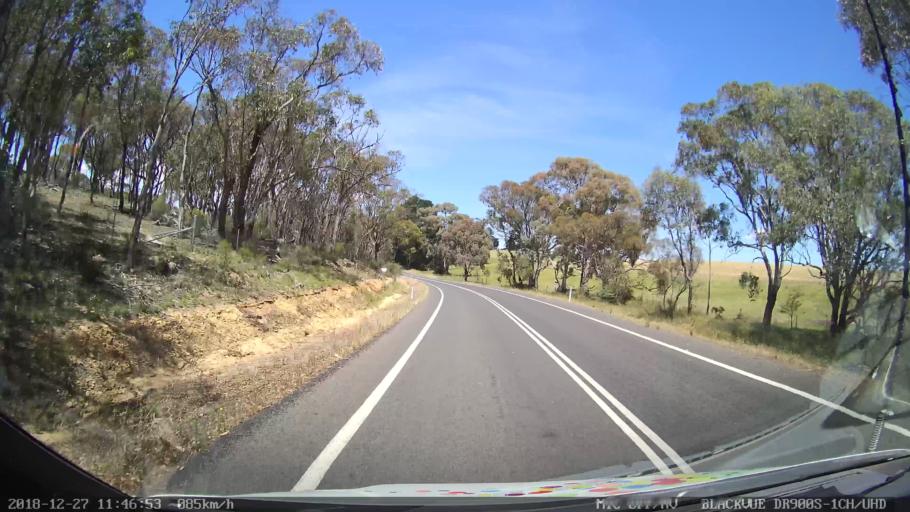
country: AU
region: New South Wales
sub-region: Bathurst Regional
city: Perthville
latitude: -33.5910
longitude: 149.4510
